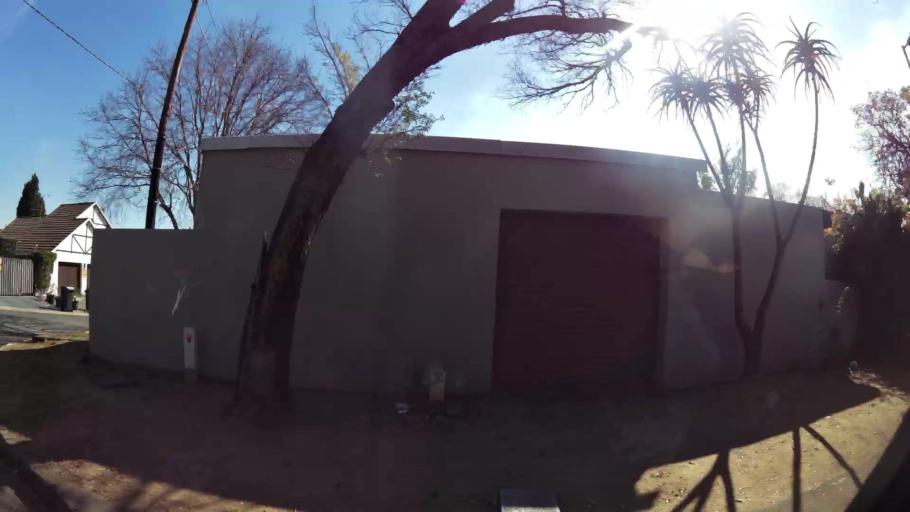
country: ZA
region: Gauteng
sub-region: City of Johannesburg Metropolitan Municipality
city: Roodepoort
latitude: -26.1052
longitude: 27.9670
